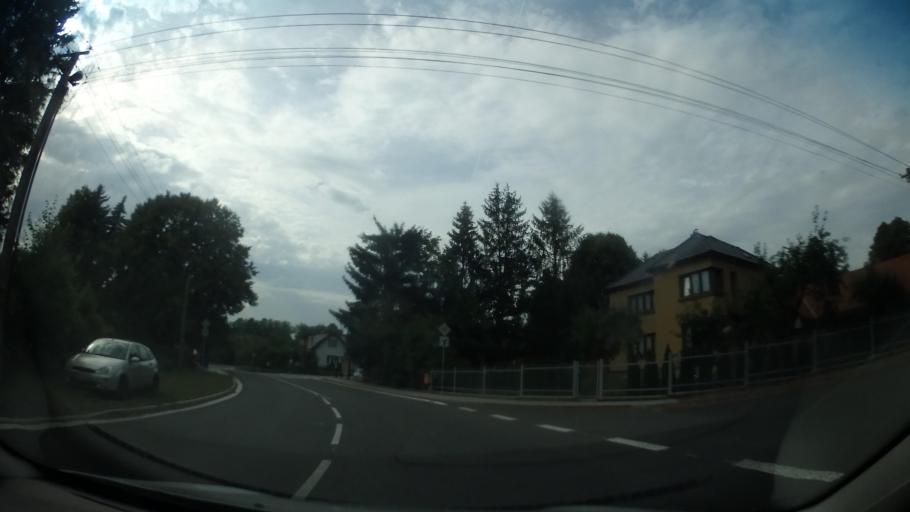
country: CZ
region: Pardubicky
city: Prachovice
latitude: 49.8685
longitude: 15.6264
